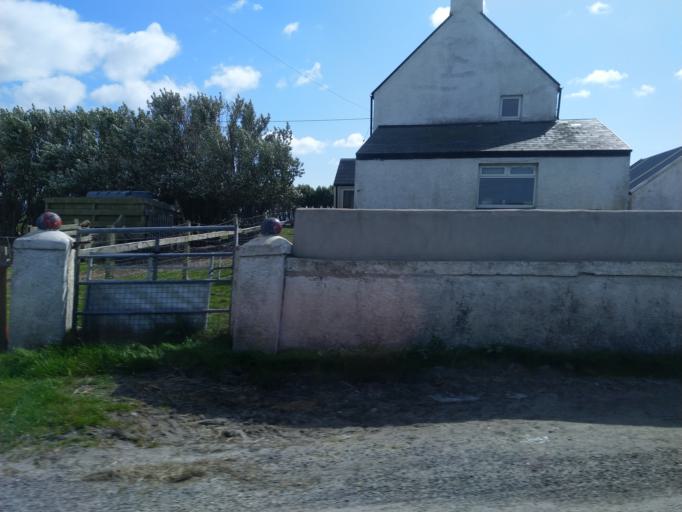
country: GB
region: Scotland
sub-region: Eilean Siar
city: Barra
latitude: 56.4818
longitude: -6.8850
